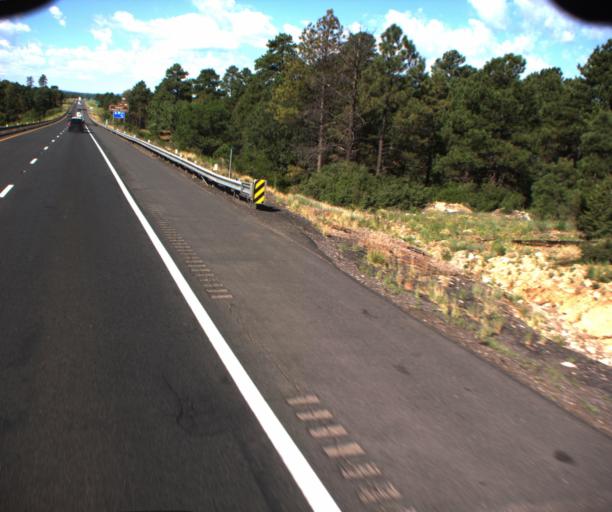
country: US
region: Arizona
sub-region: Coconino County
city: Flagstaff
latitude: 35.2001
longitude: -111.6111
